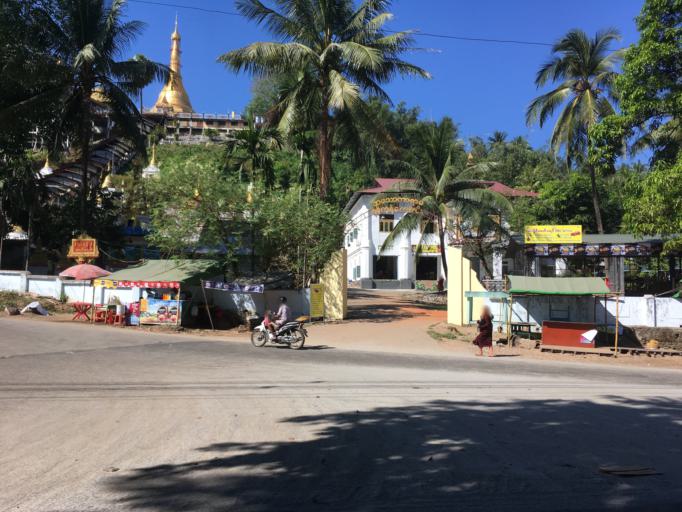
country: MM
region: Mon
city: Mawlamyine
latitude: 16.4897
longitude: 97.6303
